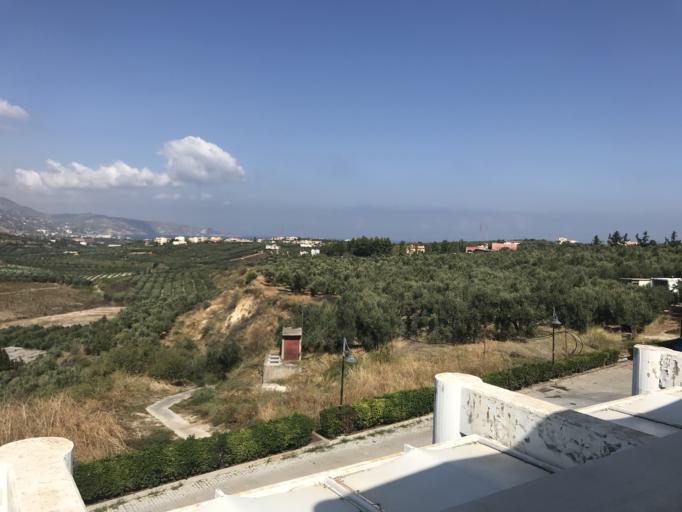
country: GR
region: Crete
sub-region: Nomos Irakleiou
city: Gazi
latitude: 35.3049
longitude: 25.0716
